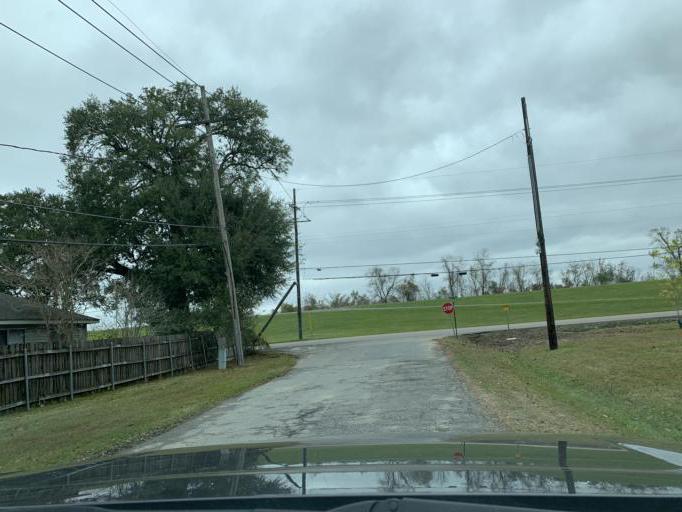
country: US
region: Louisiana
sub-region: Jefferson Parish
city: River Ridge
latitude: 29.9564
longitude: -90.2367
